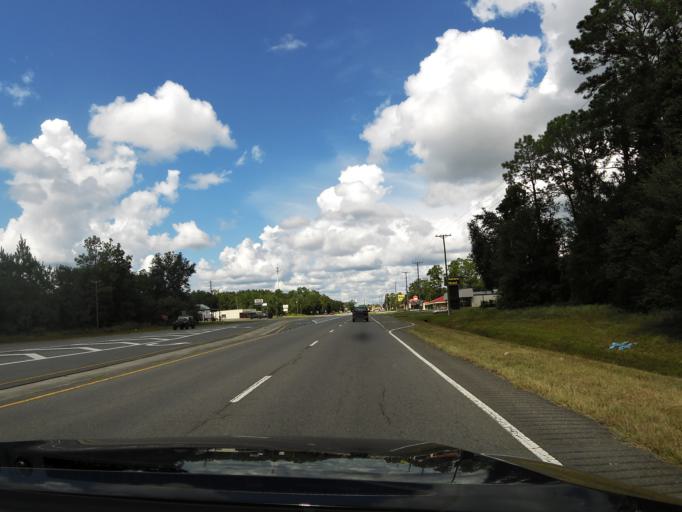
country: US
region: Georgia
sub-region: Charlton County
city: Folkston
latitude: 30.8195
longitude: -82.0014
